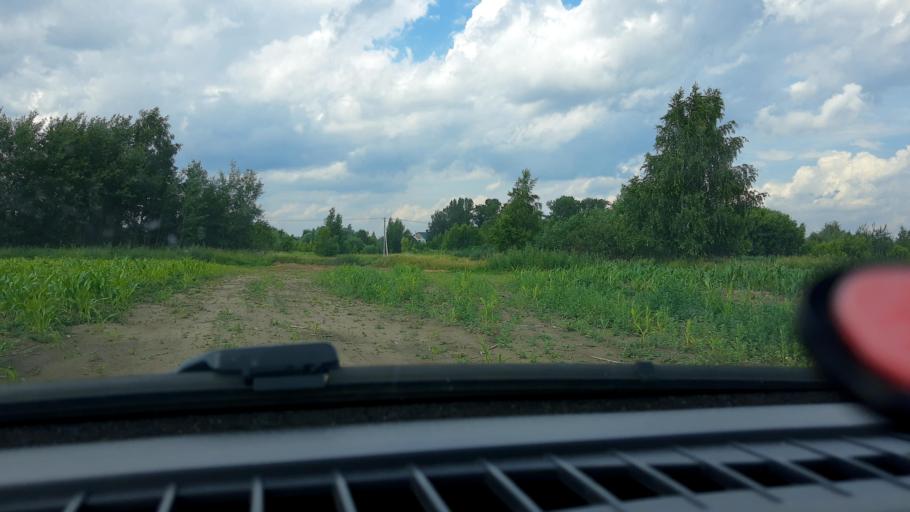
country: RU
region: Nizjnij Novgorod
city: Afonino
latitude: 56.2143
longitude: 44.1134
